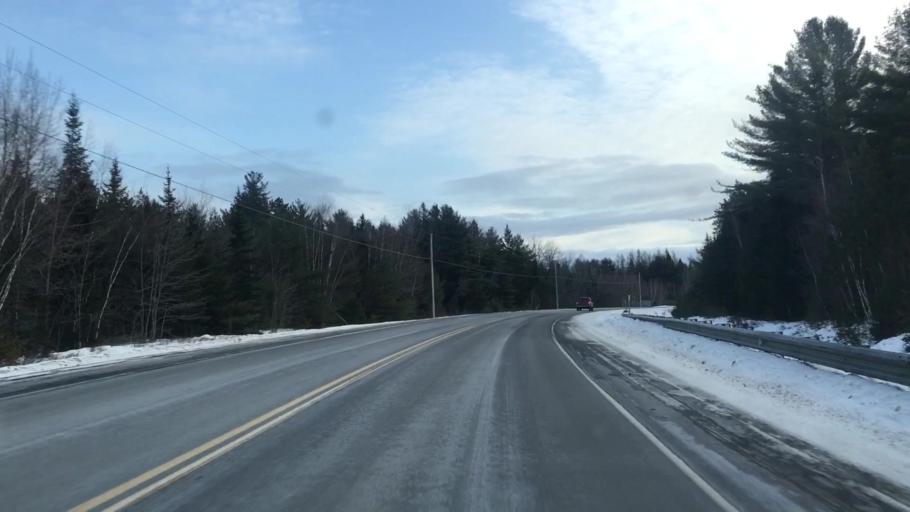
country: US
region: Maine
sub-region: Washington County
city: Addison
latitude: 44.9400
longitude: -67.7287
